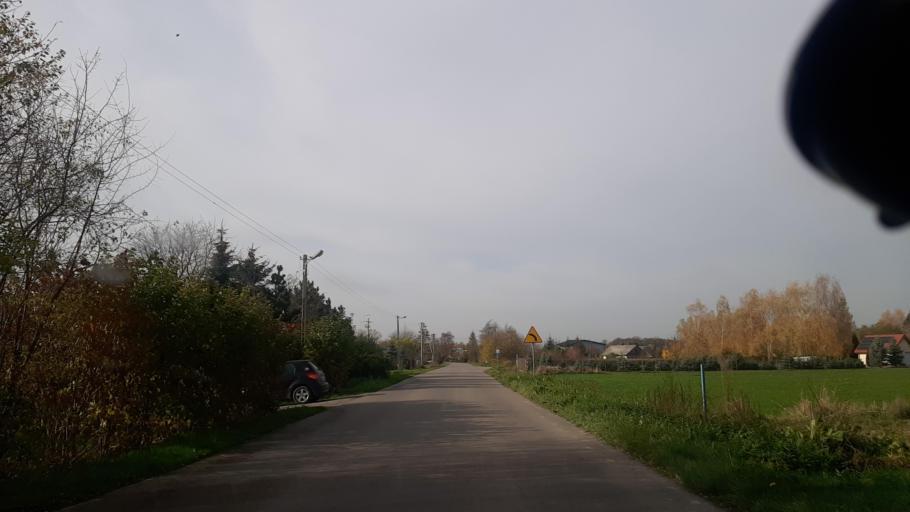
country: PL
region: Lublin Voivodeship
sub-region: Powiat lubelski
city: Jastkow
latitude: 51.3445
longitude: 22.4451
